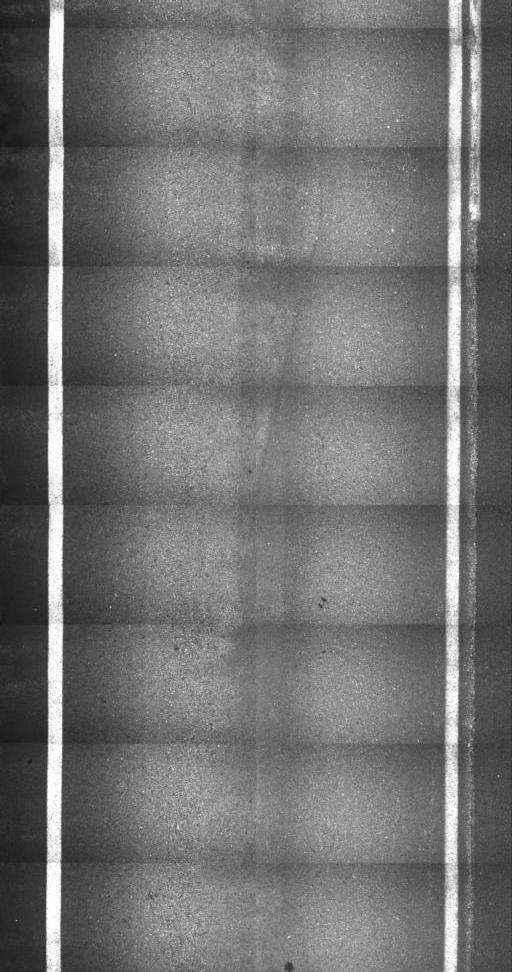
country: US
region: Vermont
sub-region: Caledonia County
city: Lyndonville
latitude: 44.6481
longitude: -72.1598
